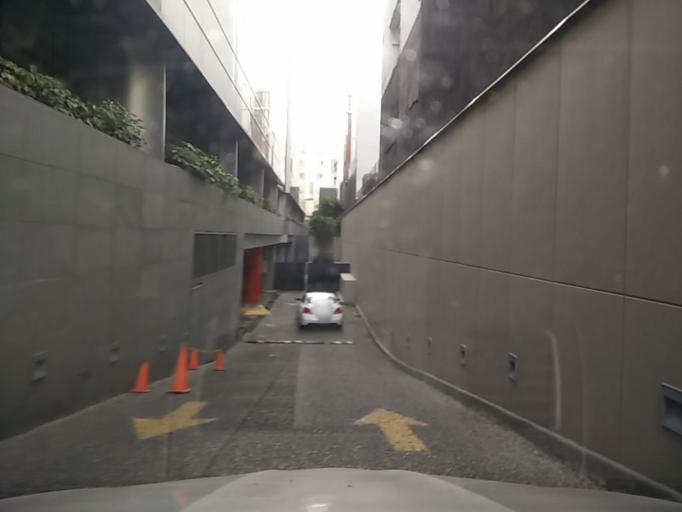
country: MX
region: Mexico City
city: Miguel Hidalgo
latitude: 19.4374
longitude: -99.1869
